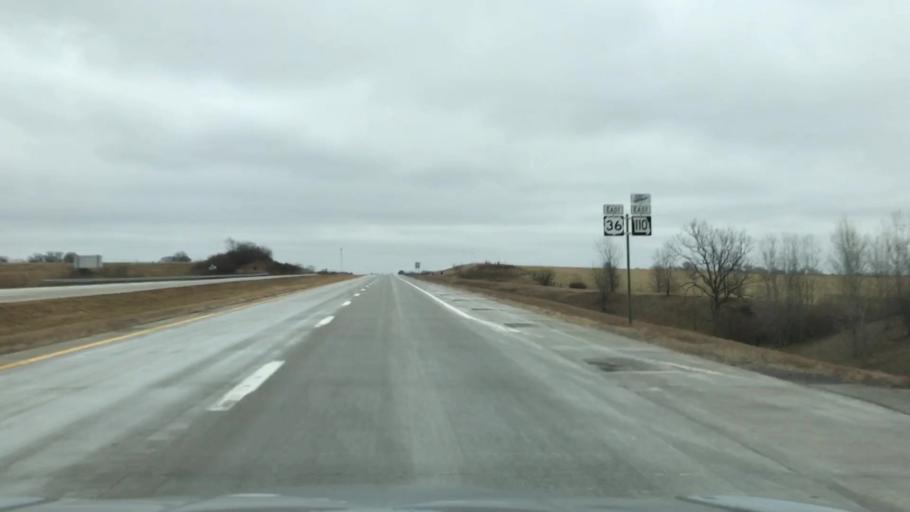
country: US
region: Missouri
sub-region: Caldwell County
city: Hamilton
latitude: 39.7349
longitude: -93.7958
